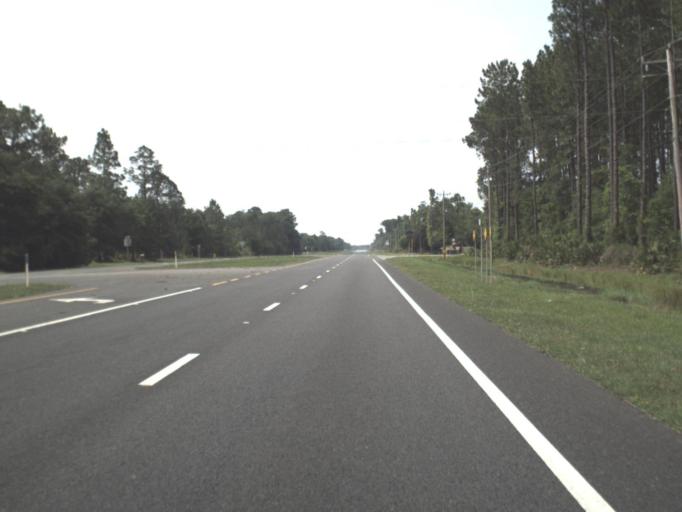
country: US
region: Florida
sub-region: Clay County
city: Green Cove Springs
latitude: 29.8515
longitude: -81.6625
